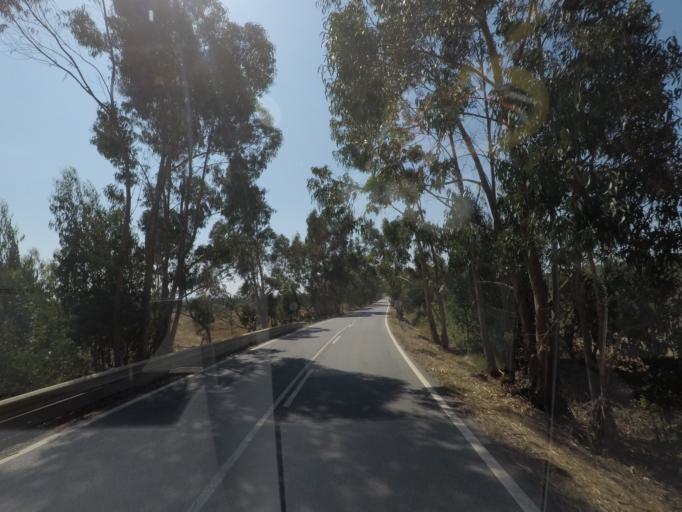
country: PT
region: Beja
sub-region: Odemira
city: Sao Teotonio
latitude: 37.5262
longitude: -8.6998
